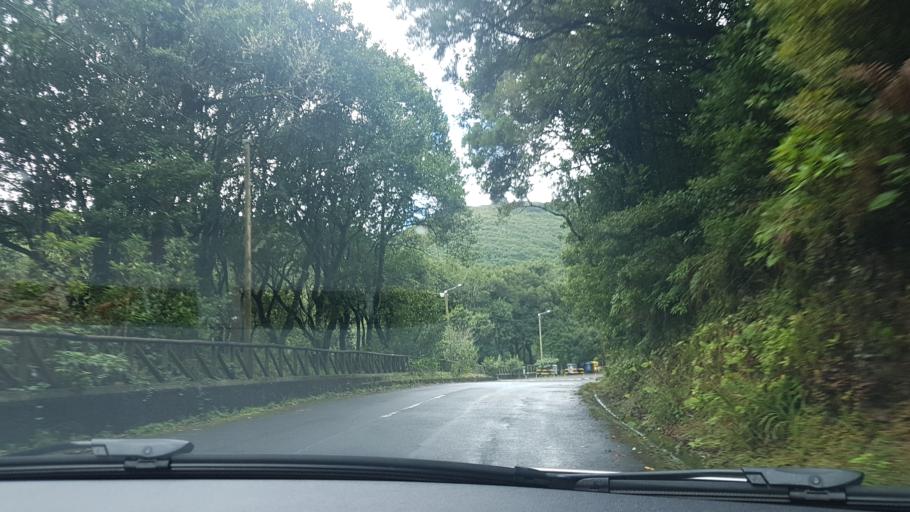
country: PT
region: Madeira
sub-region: Sao Vicente
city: Sao Vicente
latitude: 32.7608
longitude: -17.0160
